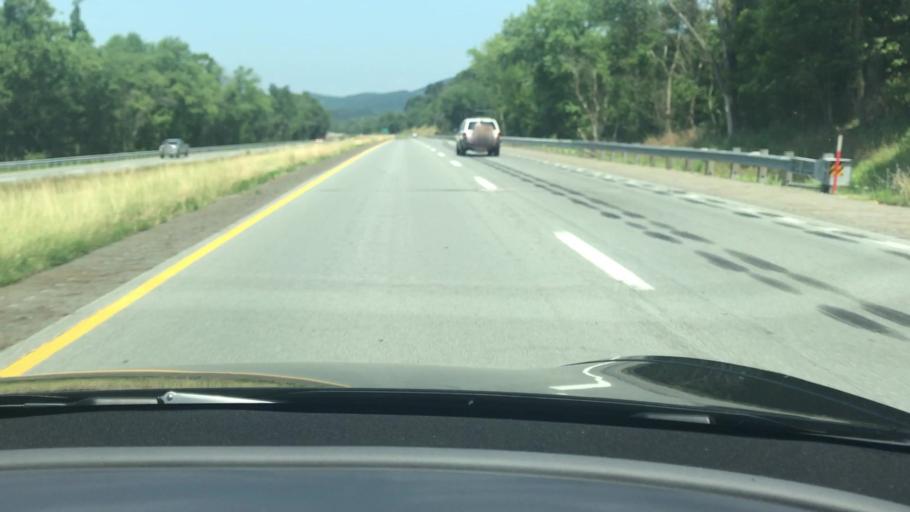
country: US
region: Pennsylvania
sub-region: Perry County
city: Newport
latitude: 40.5234
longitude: -77.1321
